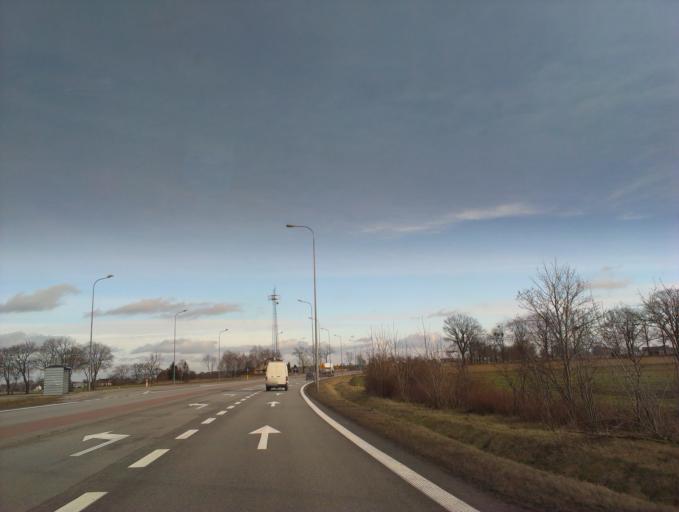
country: PL
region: Kujawsko-Pomorskie
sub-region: Powiat lipnowski
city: Kikol
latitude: 52.9340
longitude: 19.0555
